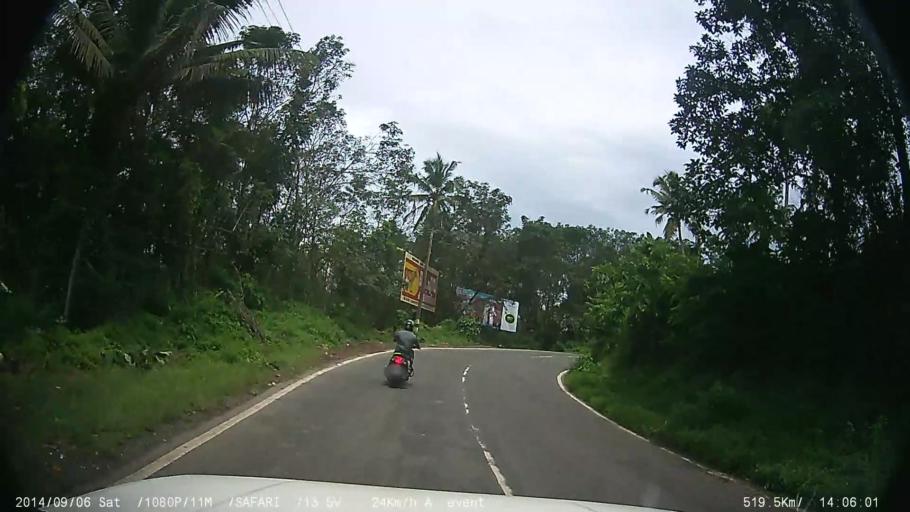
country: IN
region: Kerala
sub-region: Kottayam
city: Palackattumala
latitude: 9.7072
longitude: 76.5546
